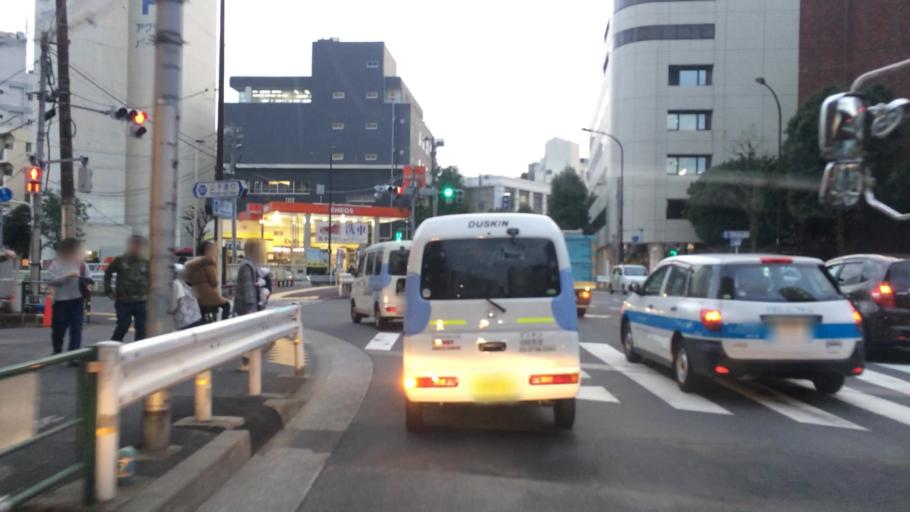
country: JP
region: Tokyo
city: Tokyo
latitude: 35.6429
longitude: 139.7009
